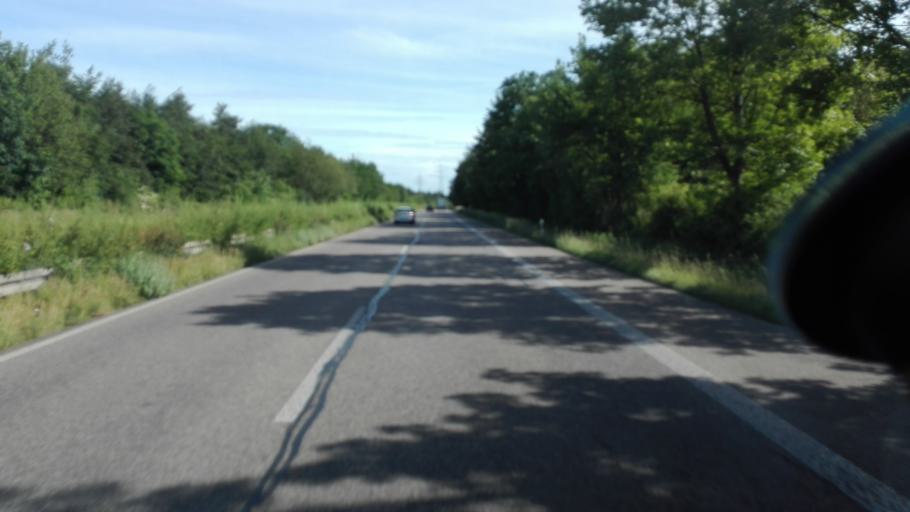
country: DE
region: Baden-Wuerttemberg
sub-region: Karlsruhe Region
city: Eggenstein-Leopoldshafen
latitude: 49.0789
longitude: 8.4080
